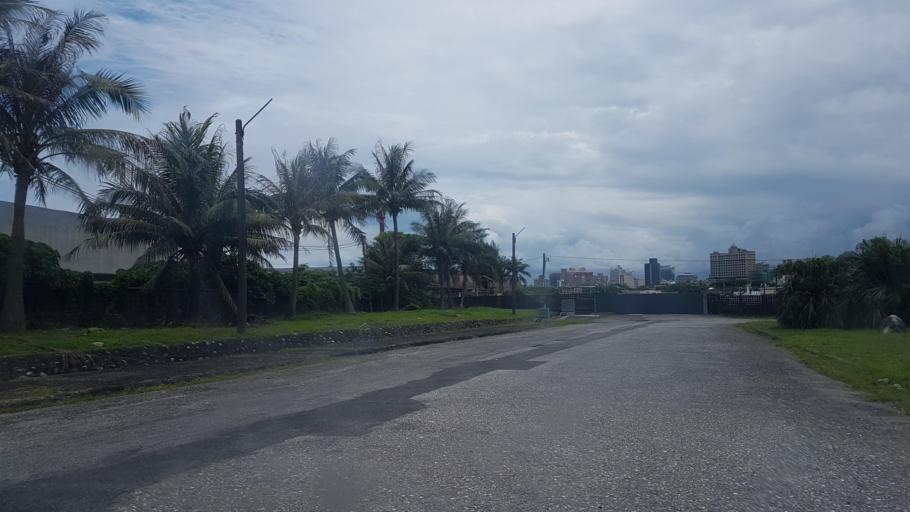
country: TW
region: Taiwan
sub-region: Hualien
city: Hualian
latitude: 24.0018
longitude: 121.6410
